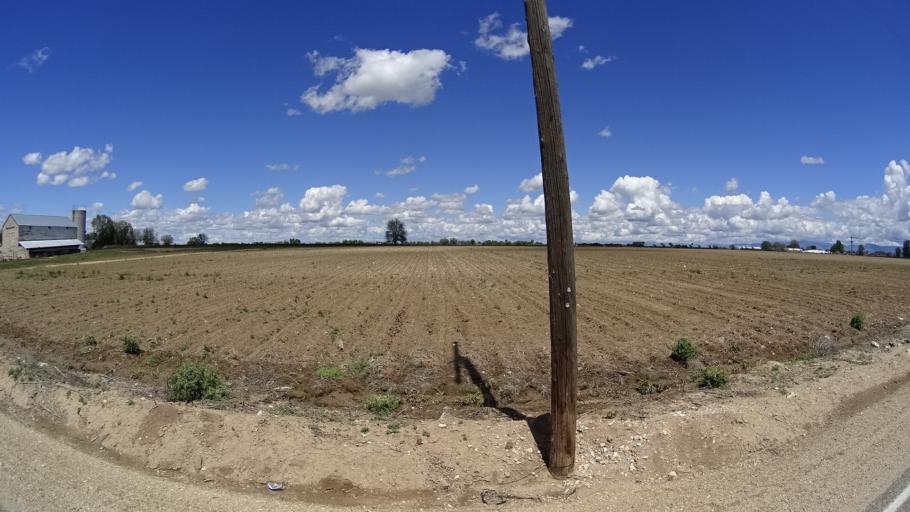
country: US
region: Idaho
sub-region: Ada County
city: Kuna
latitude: 43.5464
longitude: -116.4612
